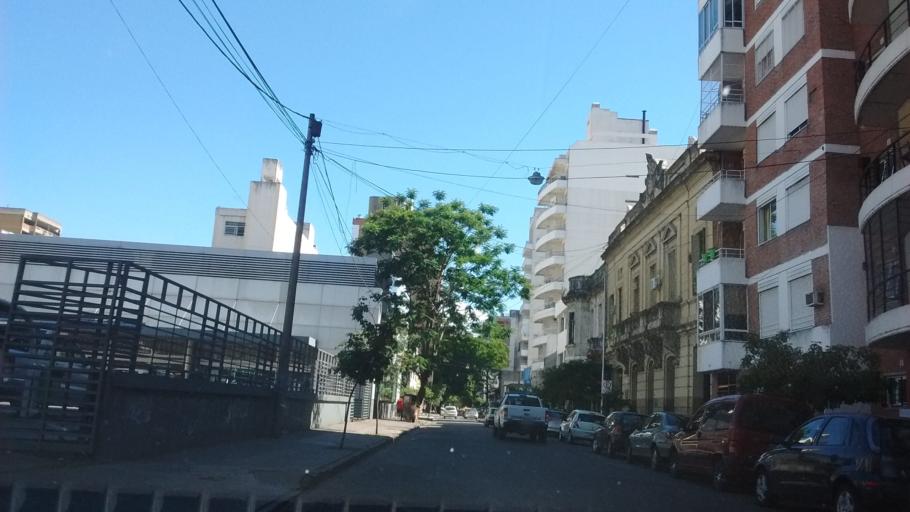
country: AR
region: Santa Fe
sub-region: Departamento de Rosario
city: Rosario
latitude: -32.9459
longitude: -60.6496
